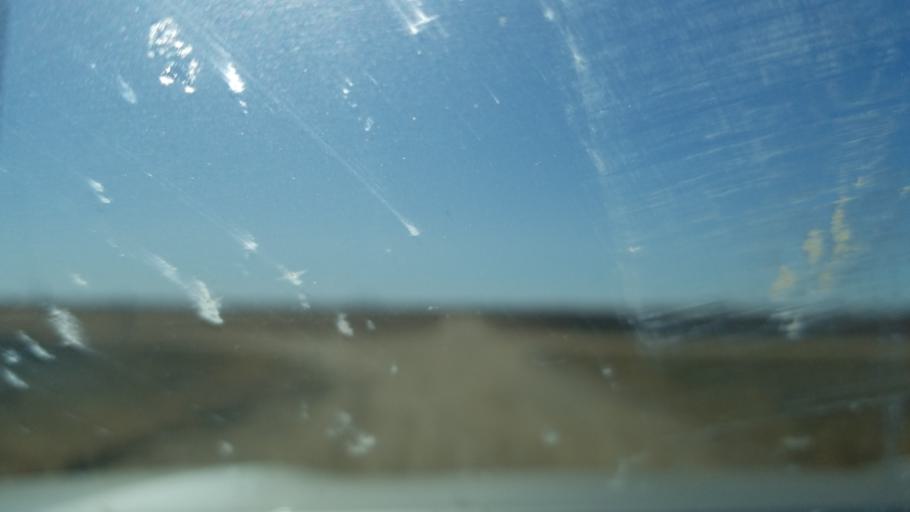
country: US
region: Kansas
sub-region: Ness County
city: Ness City
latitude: 38.5678
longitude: -99.6420
